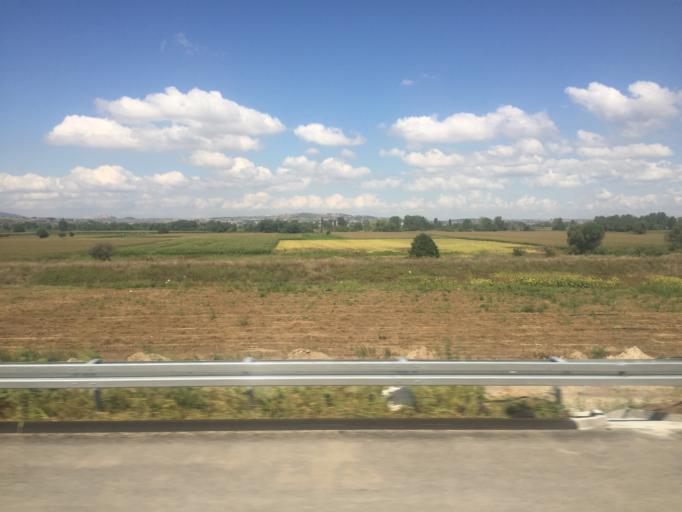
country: TR
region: Balikesir
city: Gobel
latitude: 40.0115
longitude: 28.1981
